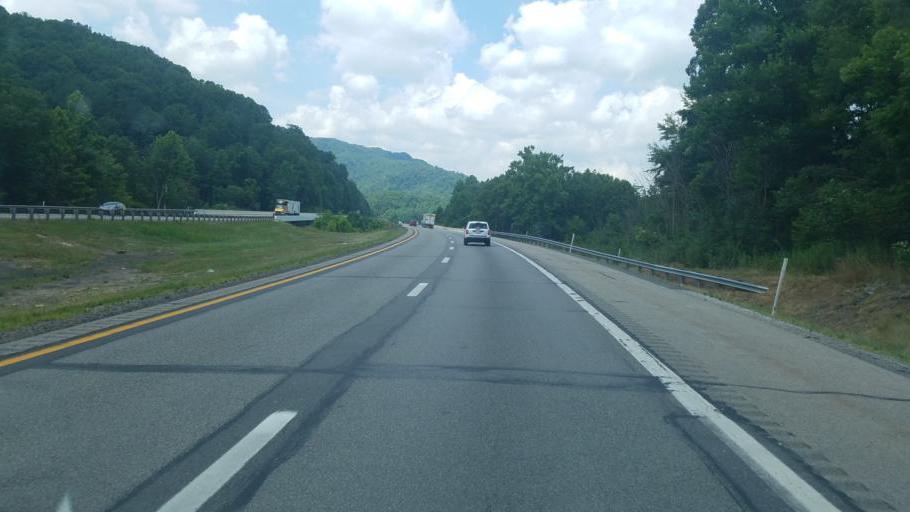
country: US
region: West Virginia
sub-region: Raleigh County
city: Bradley
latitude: 37.8702
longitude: -81.2610
